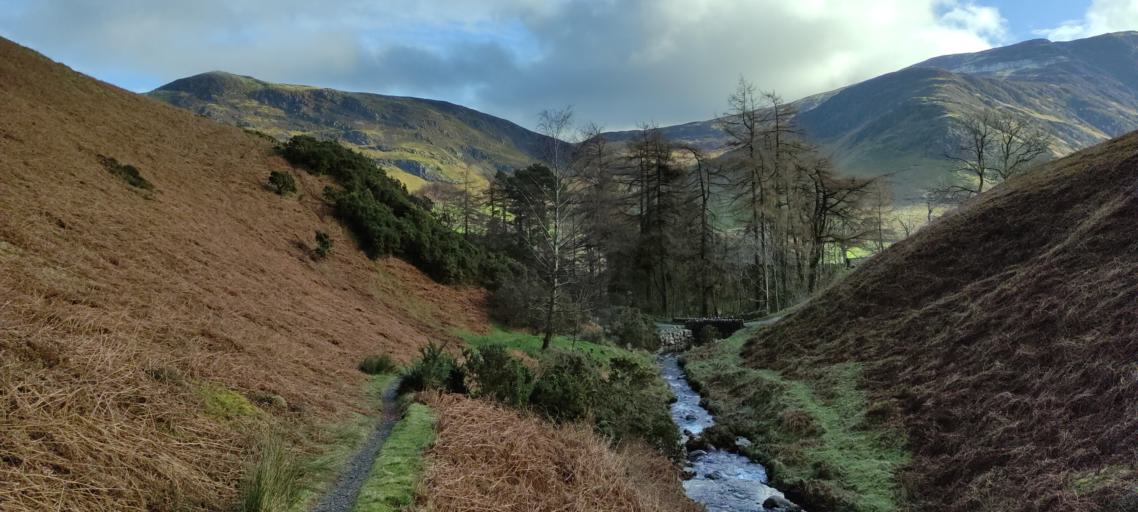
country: GB
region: England
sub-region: Cumbria
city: Keswick
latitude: 54.5713
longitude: -3.1942
